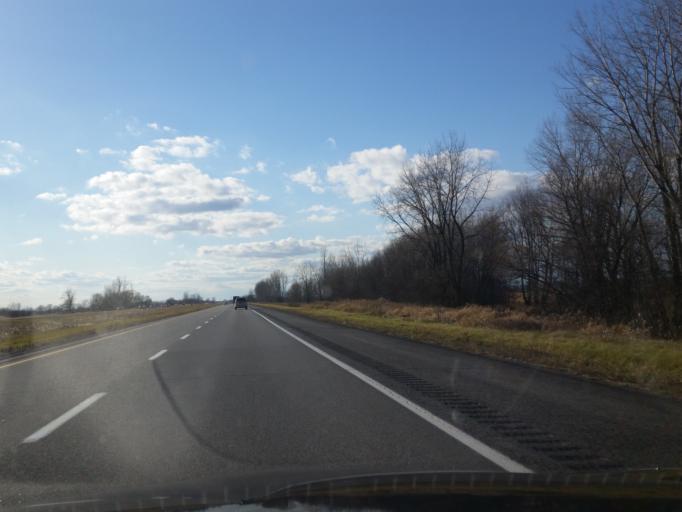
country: CA
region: Quebec
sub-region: Mauricie
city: Maskinonge
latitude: 46.1754
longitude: -73.0448
